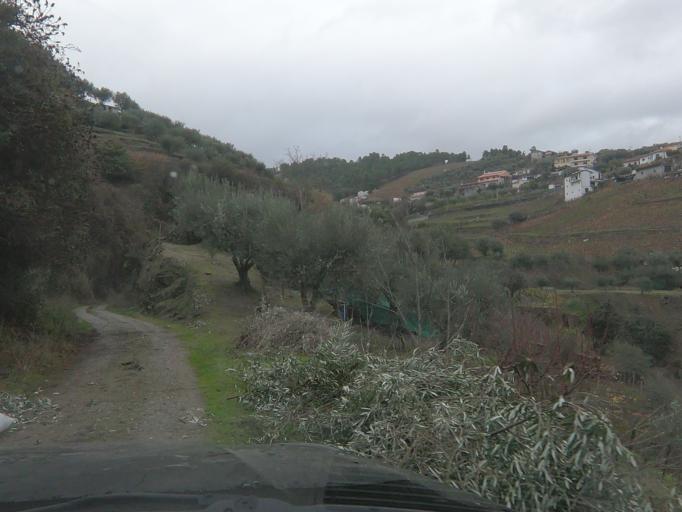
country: PT
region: Vila Real
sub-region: Vila Real
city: Vila Real
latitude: 41.2392
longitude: -7.7405
